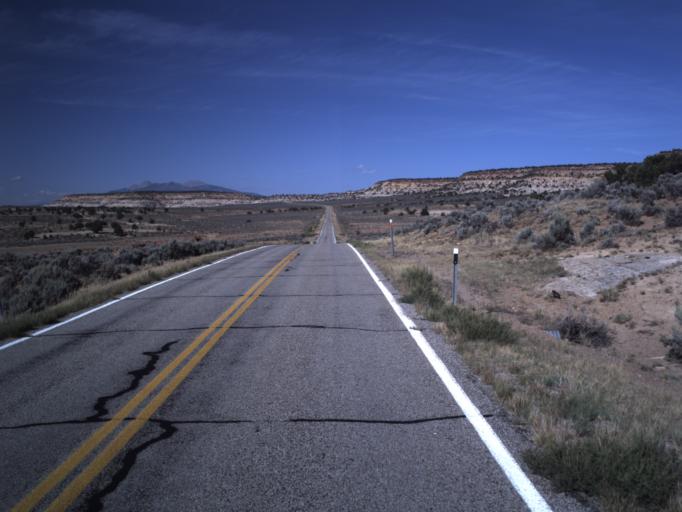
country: US
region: Utah
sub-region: San Juan County
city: Monticello
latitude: 38.0247
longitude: -109.4253
